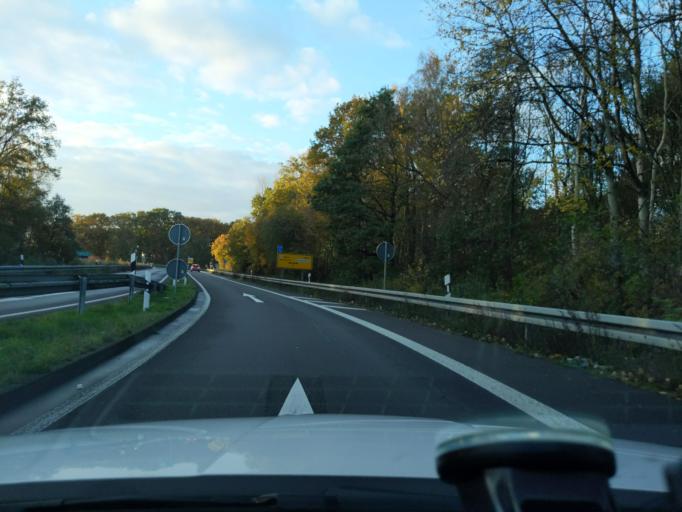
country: DE
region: North Rhine-Westphalia
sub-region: Regierungsbezirk Dusseldorf
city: Uedem
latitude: 51.6366
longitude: 6.2937
